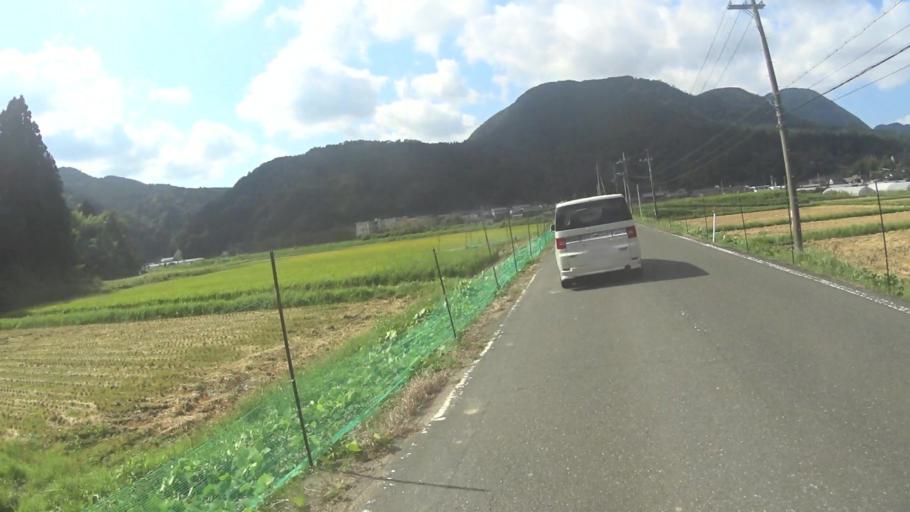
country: JP
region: Kyoto
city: Miyazu
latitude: 35.7188
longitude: 135.2565
